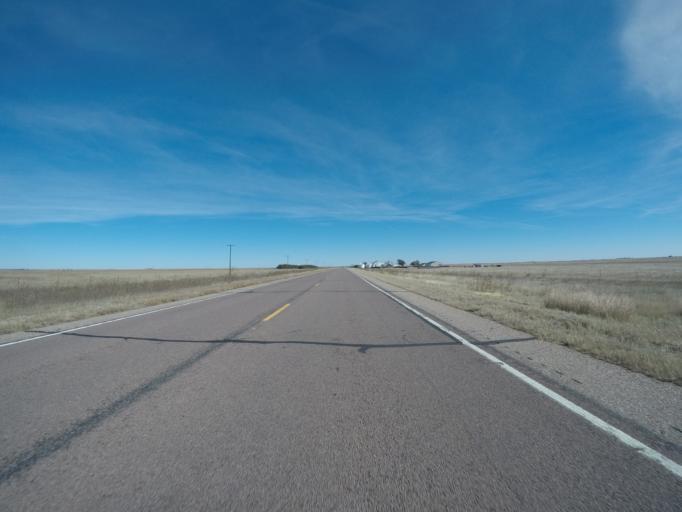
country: US
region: Colorado
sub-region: Kit Carson County
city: Burlington
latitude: 39.6569
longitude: -102.5722
